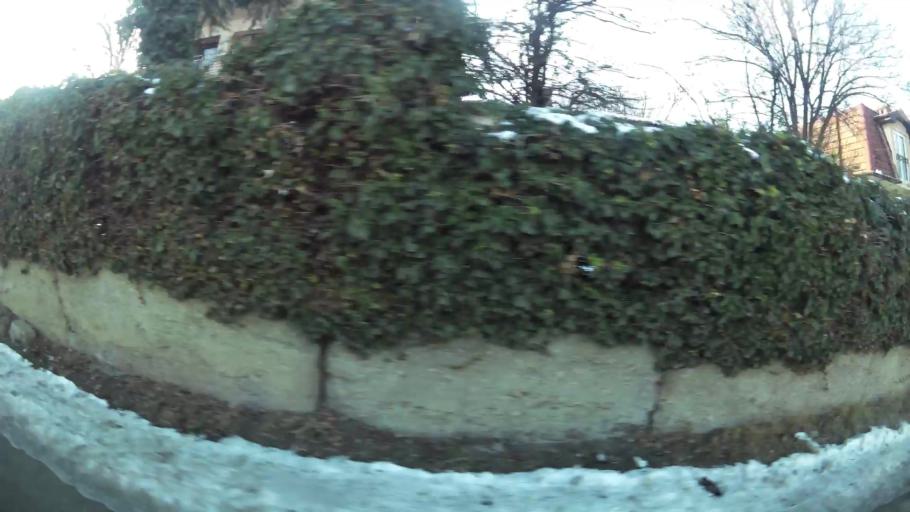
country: MK
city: Creshevo
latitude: 42.0159
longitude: 21.5098
